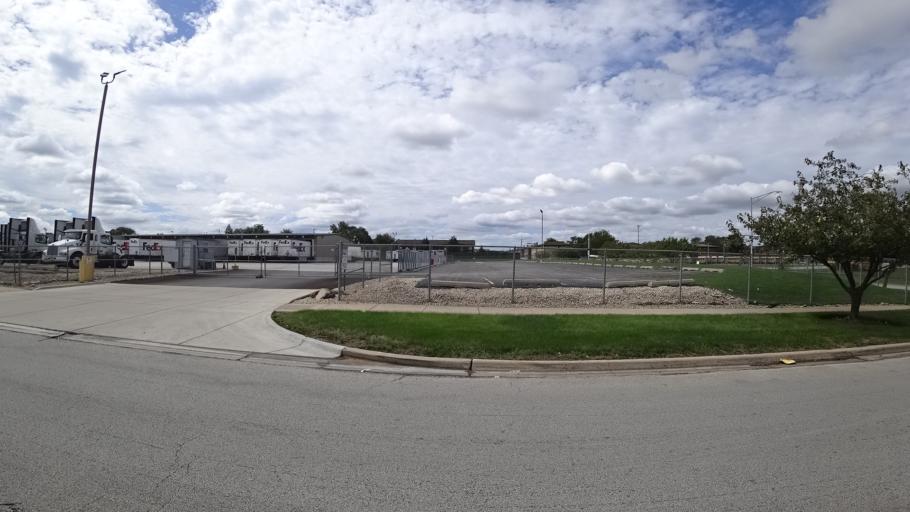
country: US
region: Illinois
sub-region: Cook County
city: Chicago Ridge
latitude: 41.7107
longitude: -87.7920
